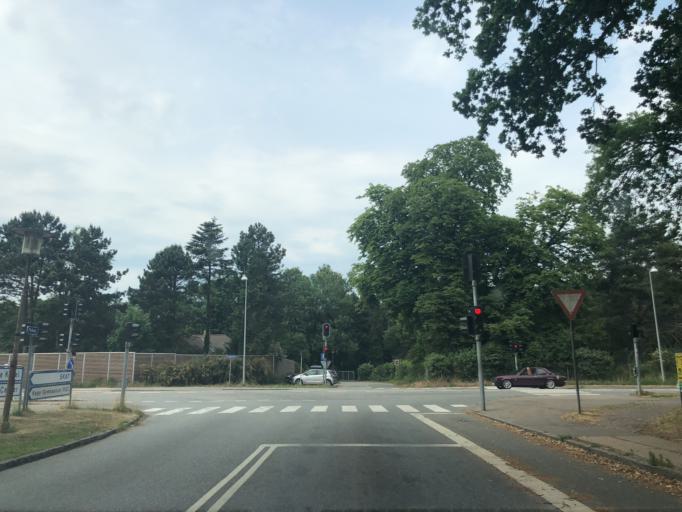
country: DK
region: Zealand
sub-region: Koge Kommune
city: Koge
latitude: 55.4561
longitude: 12.1709
